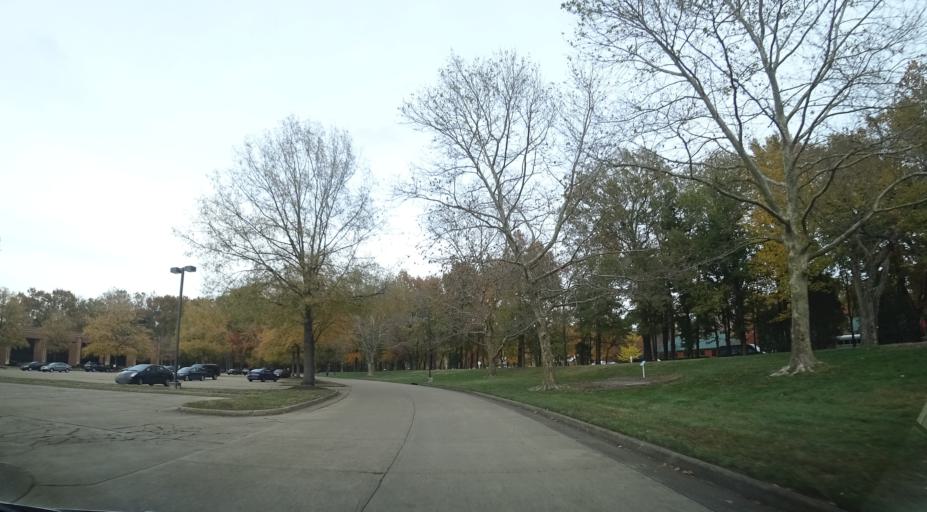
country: US
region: Virginia
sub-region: City of Hampton
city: Hampton
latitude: 37.0644
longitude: -76.4008
